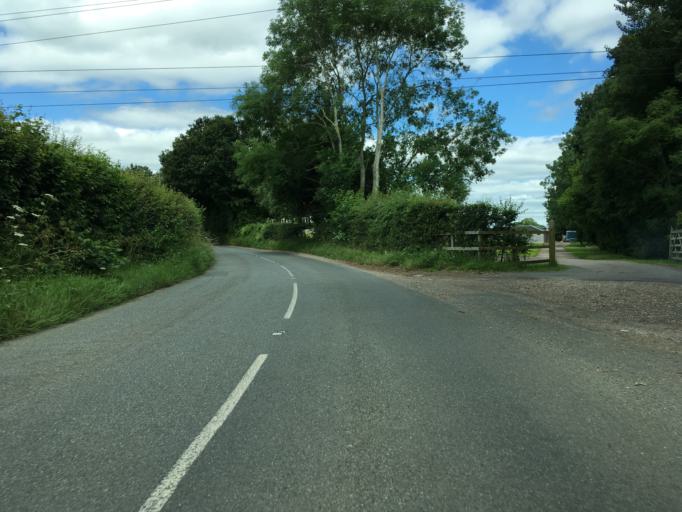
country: GB
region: England
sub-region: West Berkshire
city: Welford
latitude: 51.4332
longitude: -1.3851
